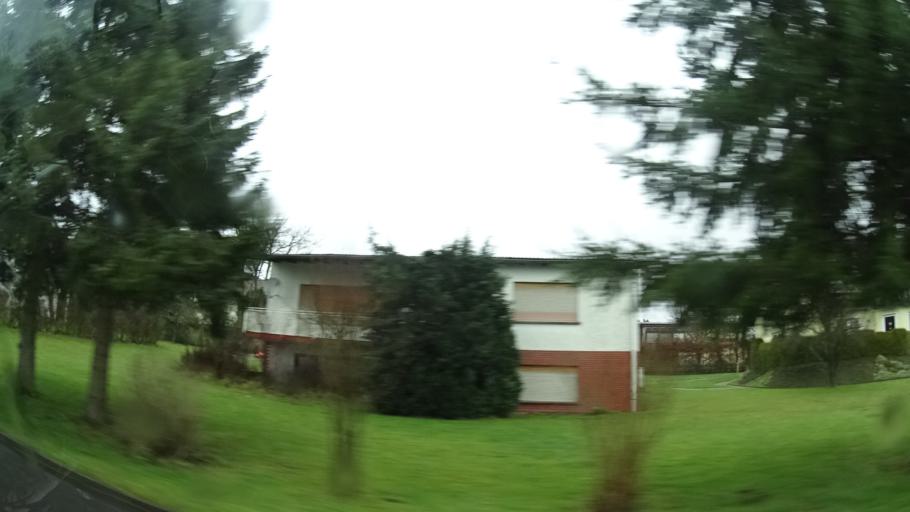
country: DE
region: Hesse
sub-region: Regierungsbezirk Kassel
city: Dipperz
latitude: 50.5658
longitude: 9.7699
